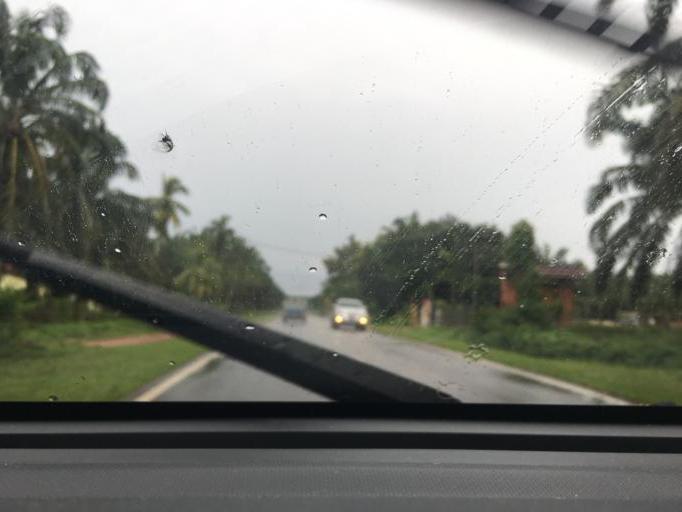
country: MY
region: Kedah
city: Sungai Petani
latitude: 5.6466
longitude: 100.6320
